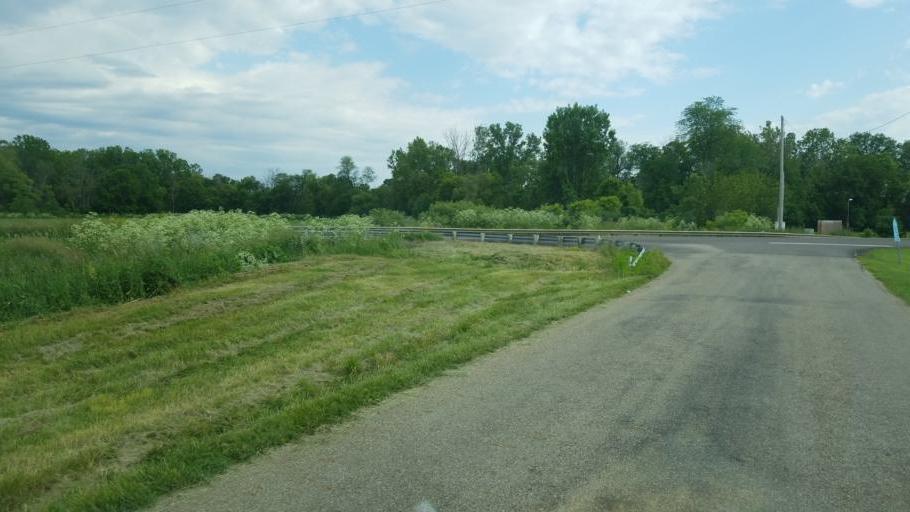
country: US
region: Ohio
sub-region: Knox County
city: Fredericktown
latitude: 40.4634
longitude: -82.6266
